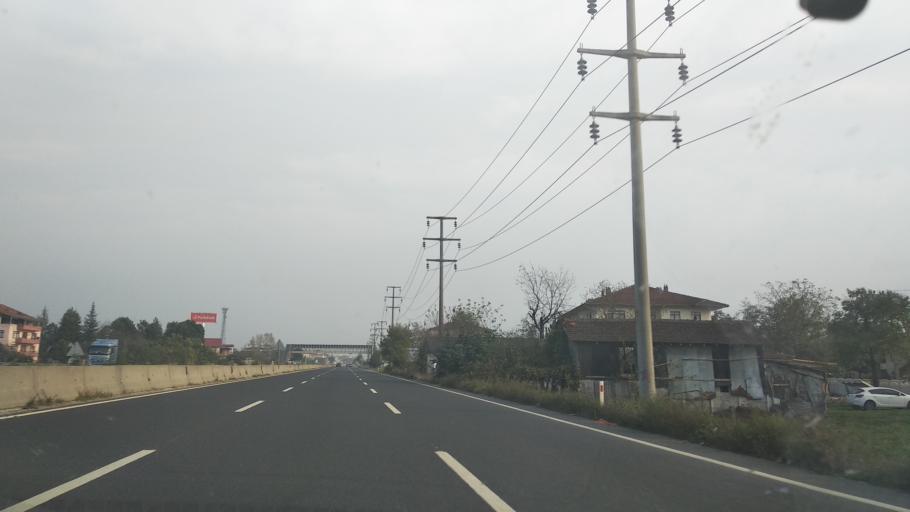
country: TR
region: Duzce
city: Duzce
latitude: 40.8071
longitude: 31.2299
